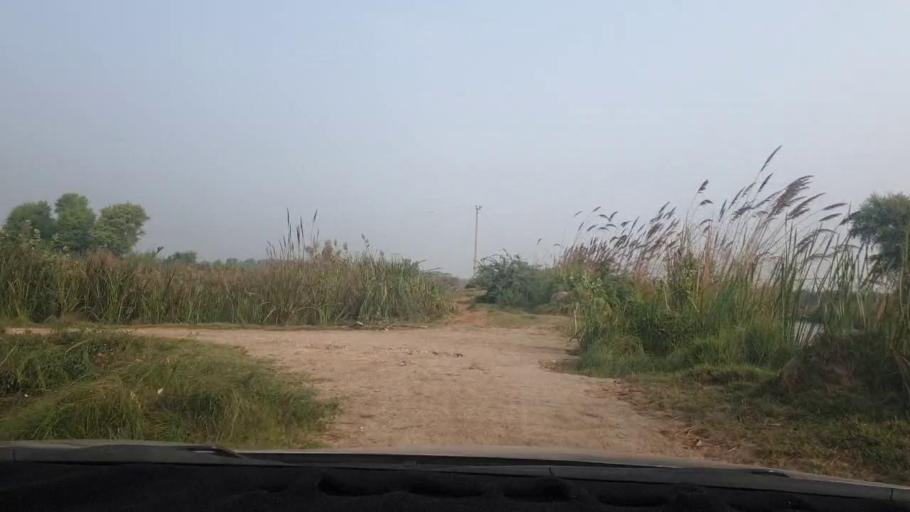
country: PK
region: Sindh
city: Matiari
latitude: 25.6008
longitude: 68.5512
